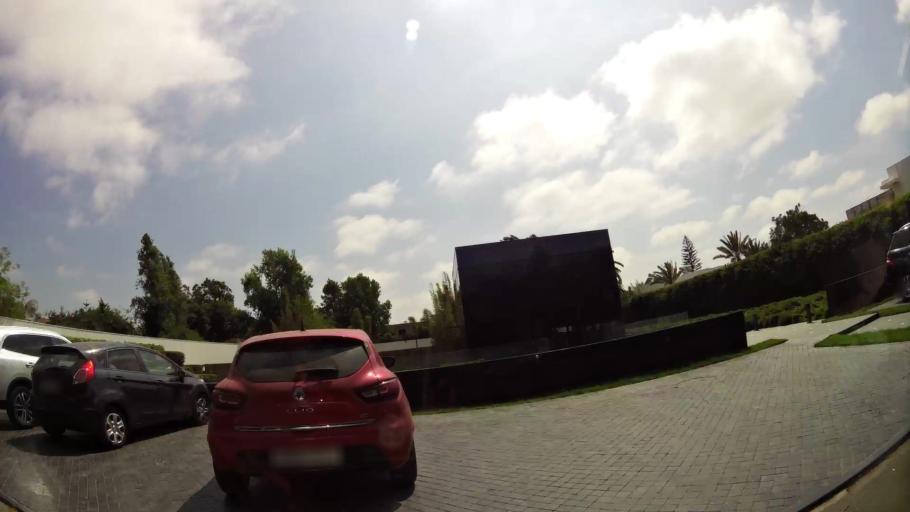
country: MA
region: Rabat-Sale-Zemmour-Zaer
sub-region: Rabat
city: Rabat
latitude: 33.9804
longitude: -6.8364
